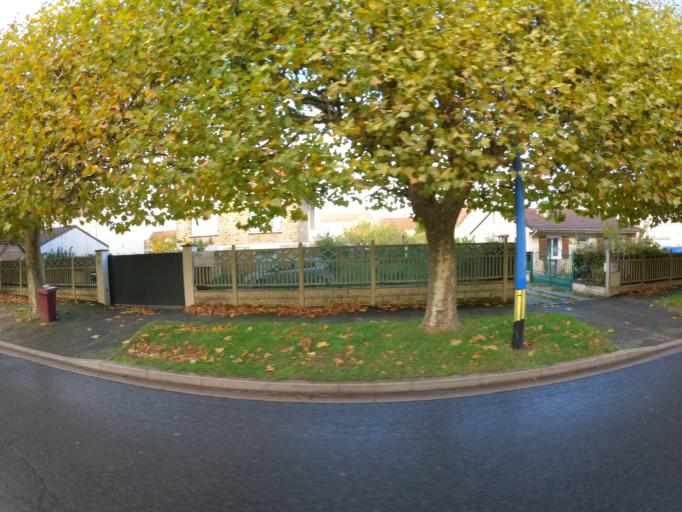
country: FR
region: Ile-de-France
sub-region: Departement de Seine-et-Marne
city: Brou-sur-Chantereine
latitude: 48.8946
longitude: 2.6185
